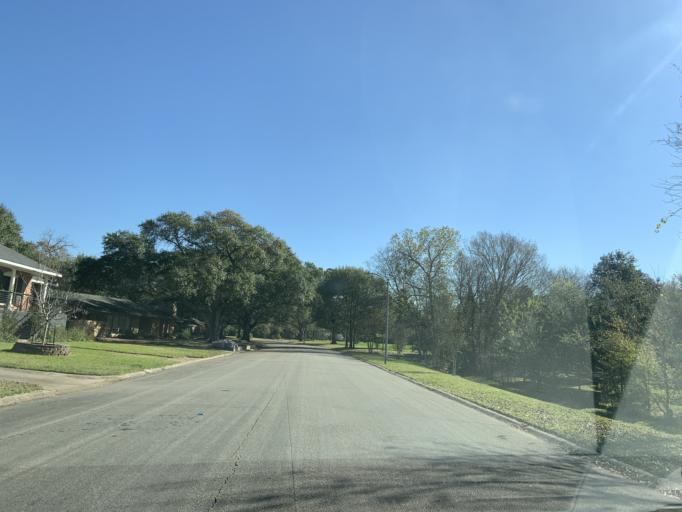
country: US
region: Texas
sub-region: Fort Bend County
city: Missouri City
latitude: 29.6774
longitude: -95.5167
